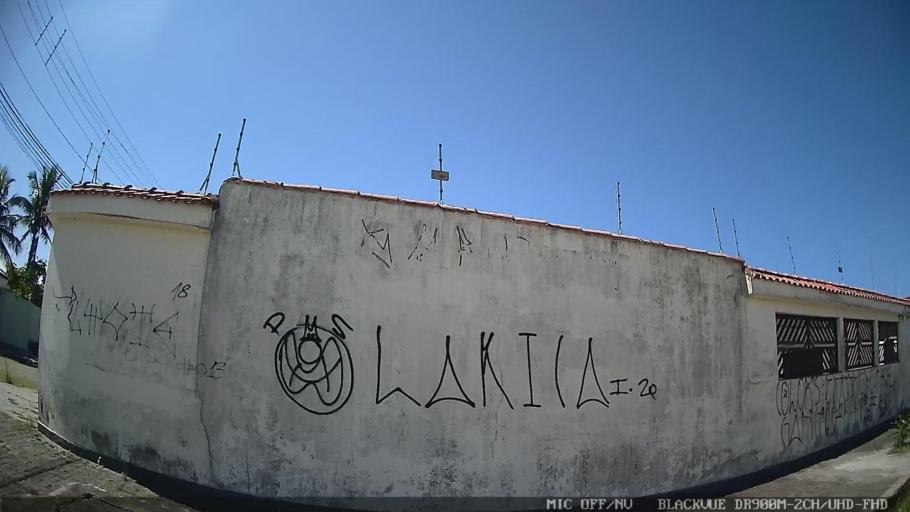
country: BR
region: Sao Paulo
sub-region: Peruibe
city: Peruibe
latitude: -24.3146
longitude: -46.9888
